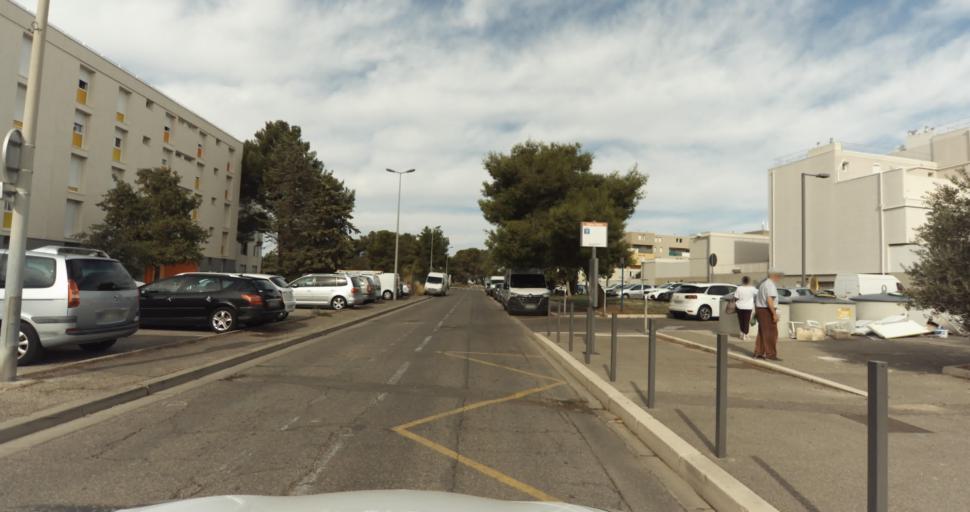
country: FR
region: Provence-Alpes-Cote d'Azur
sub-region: Departement des Bouches-du-Rhone
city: Miramas
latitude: 43.5951
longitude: 5.0080
